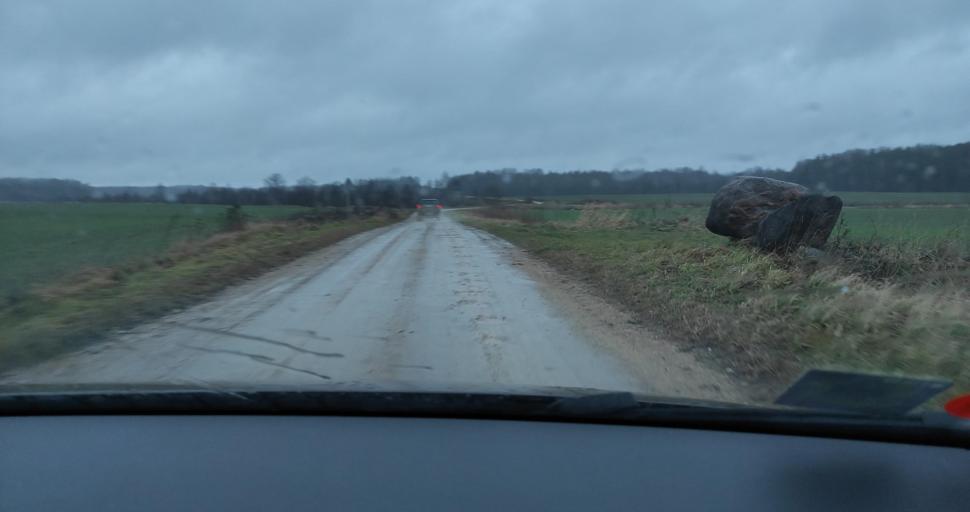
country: LV
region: Skrunda
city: Skrunda
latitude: 56.6254
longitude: 22.2362
